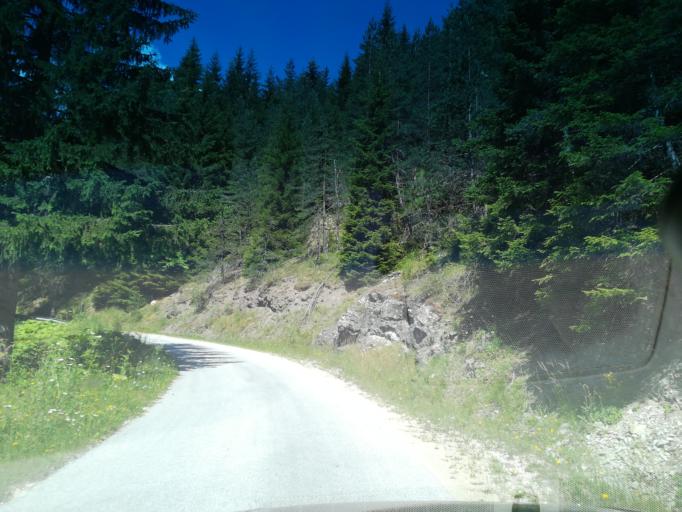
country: BG
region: Smolyan
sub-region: Obshtina Chepelare
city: Chepelare
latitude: 41.6701
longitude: 24.7957
